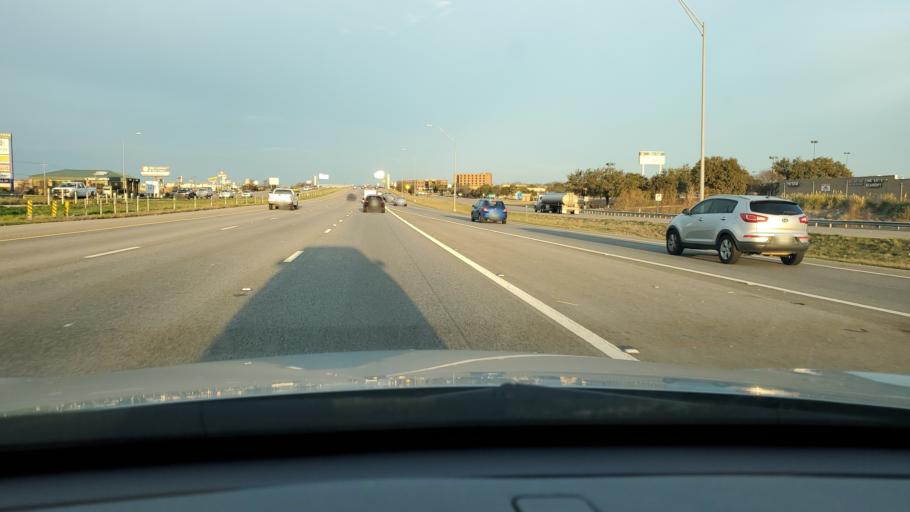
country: US
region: Texas
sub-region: Bell County
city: Killeen
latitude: 31.0887
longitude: -97.7152
